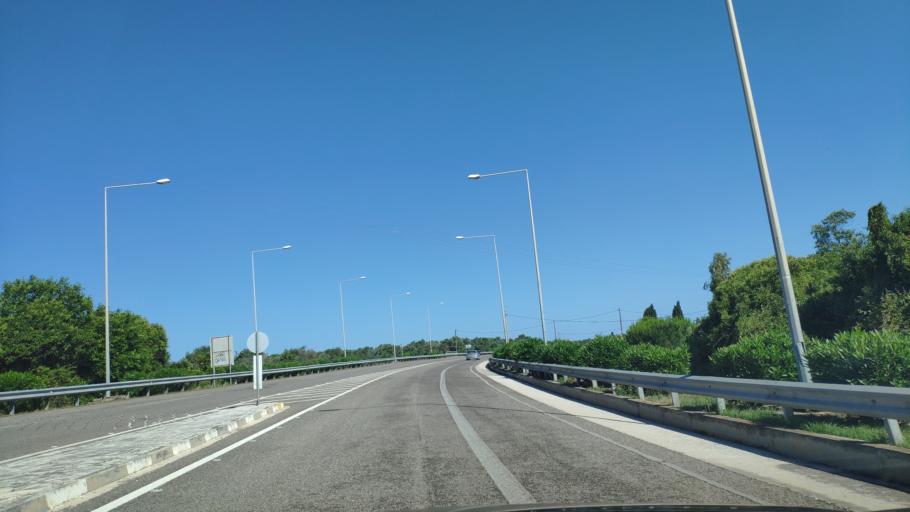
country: GR
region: Epirus
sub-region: Nomos Prevezis
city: Preveza
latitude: 38.9499
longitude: 20.7361
